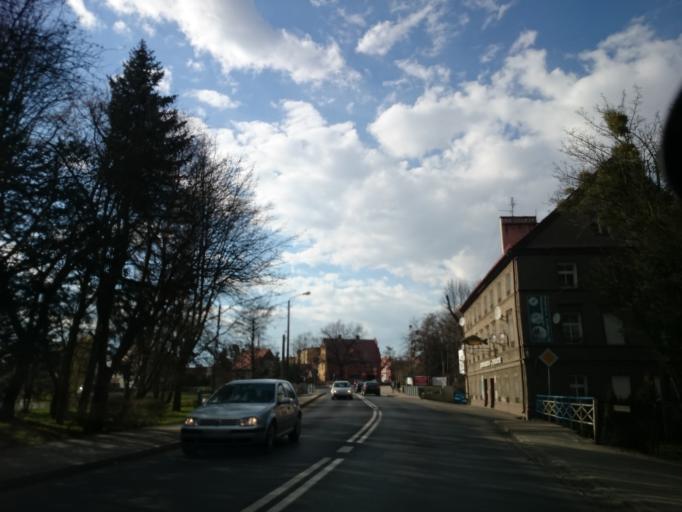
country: PL
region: Opole Voivodeship
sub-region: Powiat opolski
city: Niemodlin
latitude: 50.6409
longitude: 17.6242
